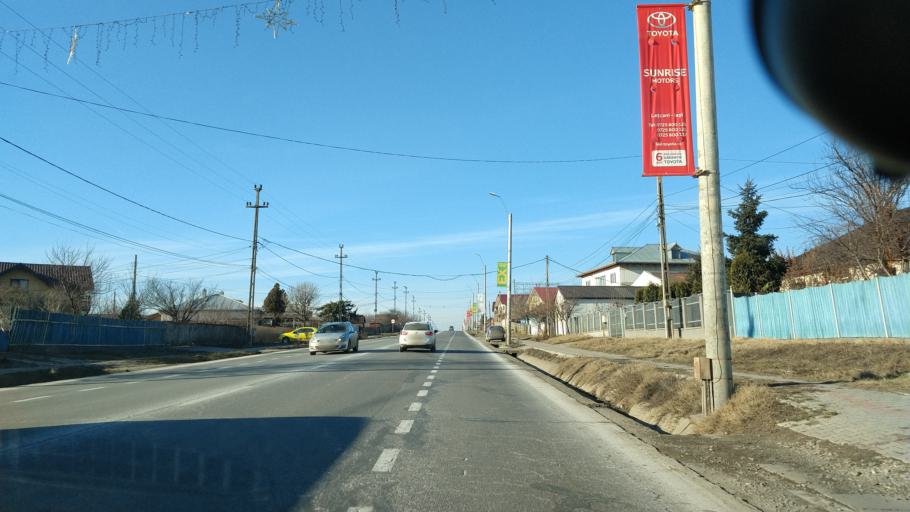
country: RO
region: Iasi
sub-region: Comuna Letcani
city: Letcani
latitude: 47.1915
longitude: 27.4265
